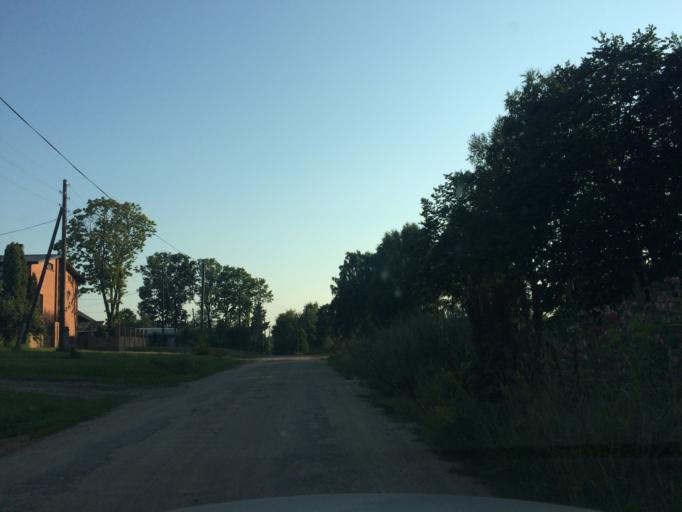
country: LV
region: Rezekne
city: Rezekne
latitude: 56.5090
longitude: 27.3509
